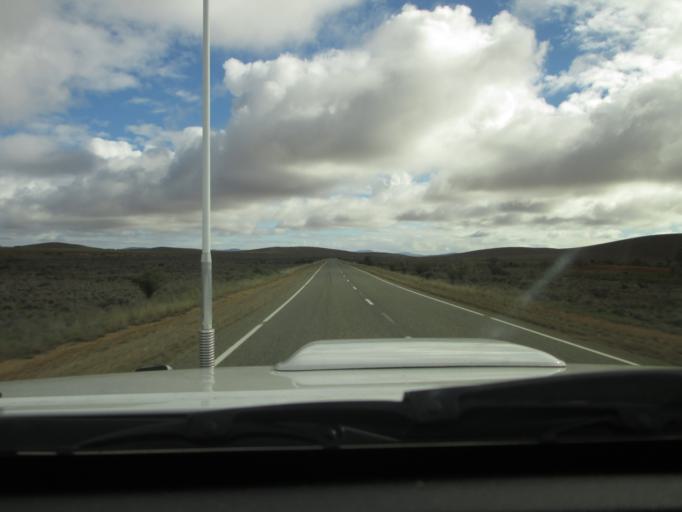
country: AU
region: South Australia
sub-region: Flinders Ranges
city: Quorn
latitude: -32.1550
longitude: 138.5267
